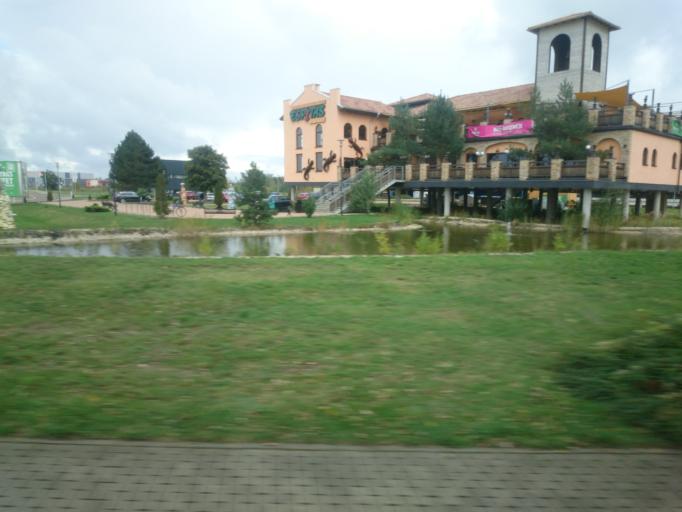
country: DE
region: Saxony-Anhalt
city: Dieskau
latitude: 51.4488
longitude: 12.0231
